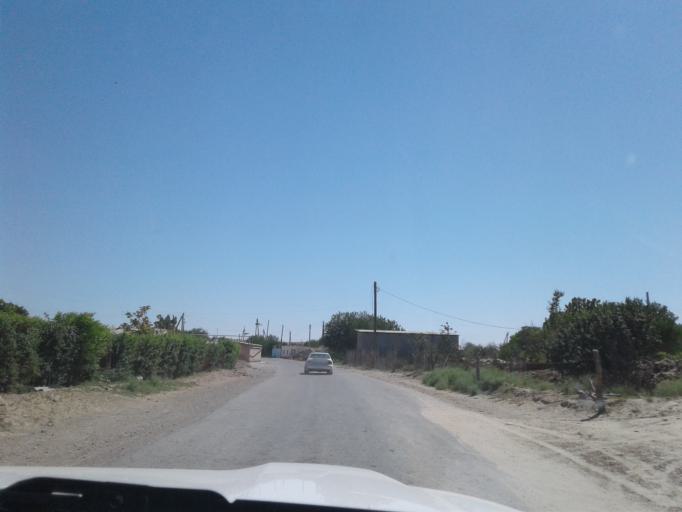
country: AF
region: Badghis
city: Bala Murghab
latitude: 35.9588
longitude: 62.9063
